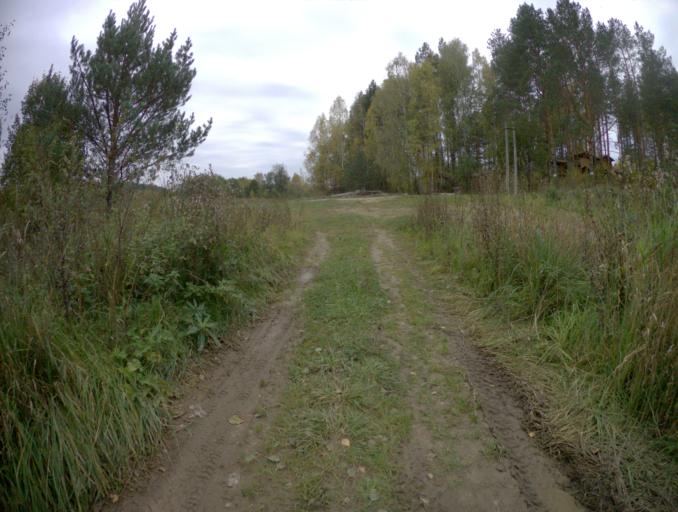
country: RU
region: Vladimir
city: Mstera
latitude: 56.3594
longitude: 41.8683
